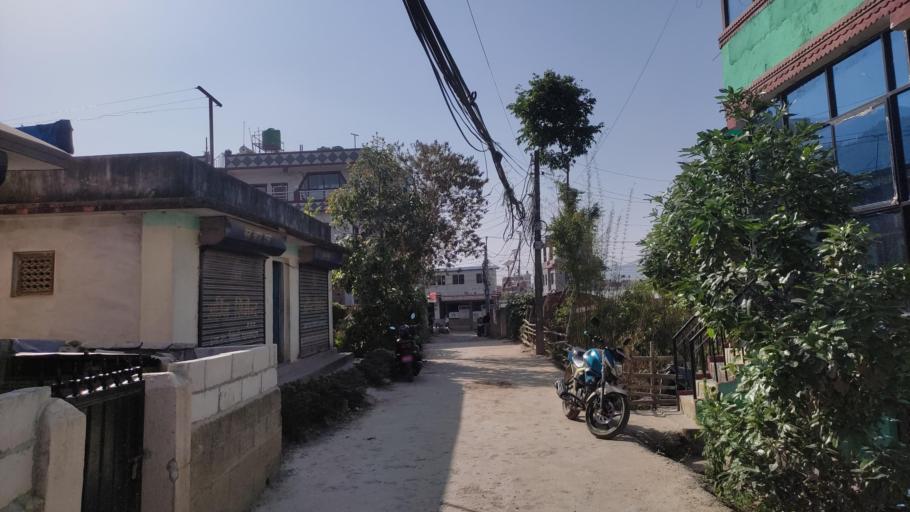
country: NP
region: Central Region
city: Kirtipur
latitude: 27.6660
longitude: 85.2662
